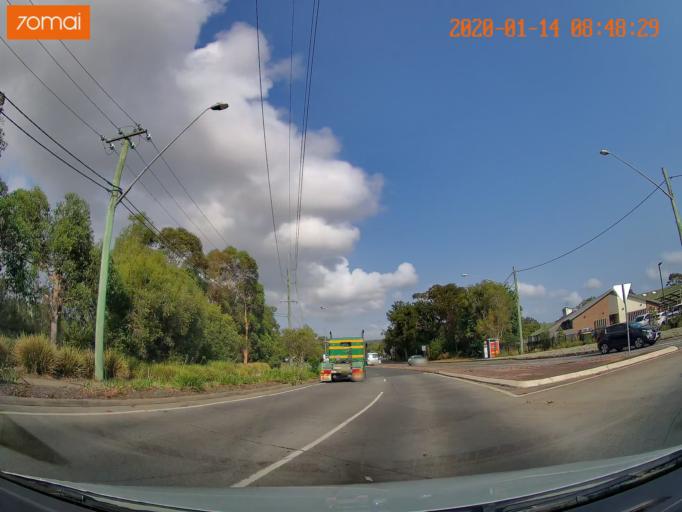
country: AU
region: New South Wales
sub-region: Wyong Shire
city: Tumbi Vmbi
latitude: -33.3642
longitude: 151.4541
